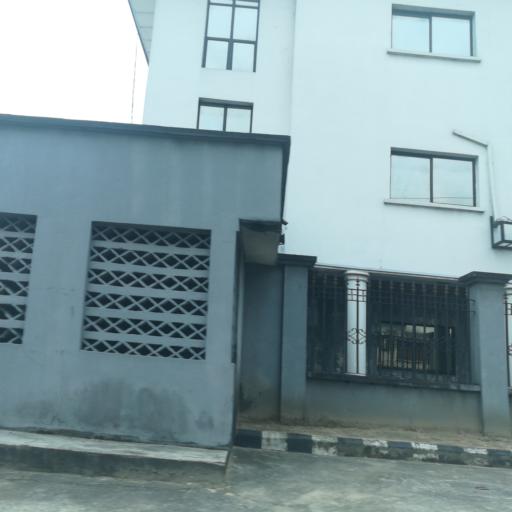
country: NG
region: Rivers
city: Port Harcourt
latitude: 4.7959
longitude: 7.0063
